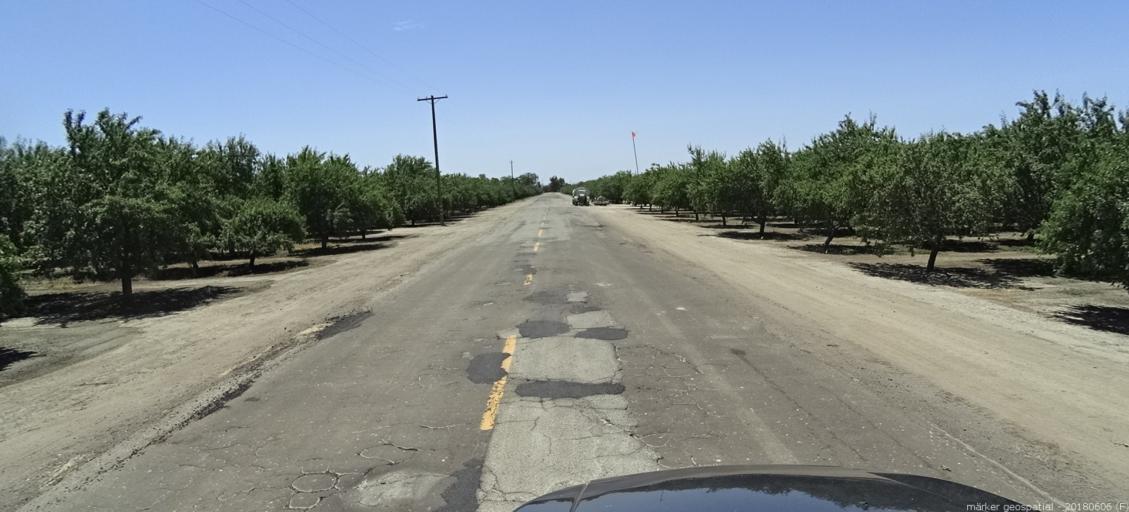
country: US
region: California
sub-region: Fresno County
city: Firebaugh
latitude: 36.8488
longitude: -120.4179
